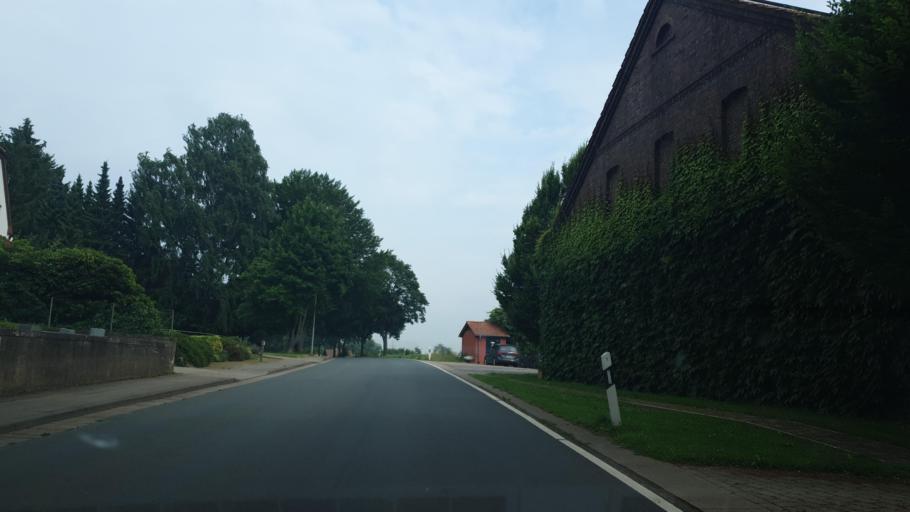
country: DE
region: North Rhine-Westphalia
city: Bad Oeynhausen
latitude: 52.2510
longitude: 8.7851
